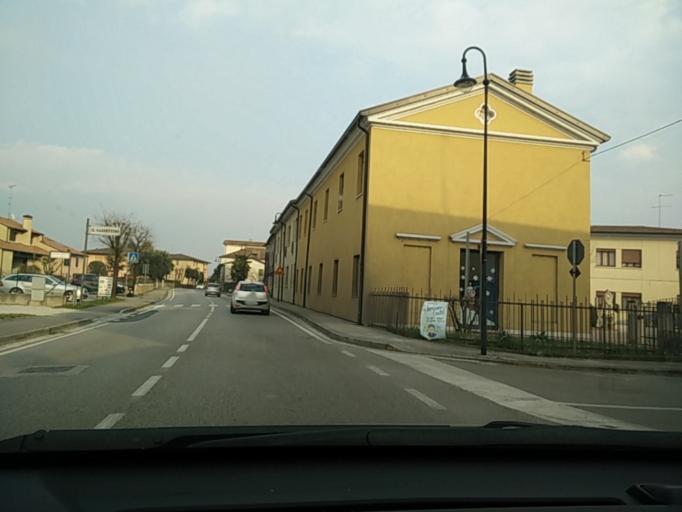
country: IT
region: Veneto
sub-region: Provincia di Treviso
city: Ormelle
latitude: 45.7788
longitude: 12.4212
